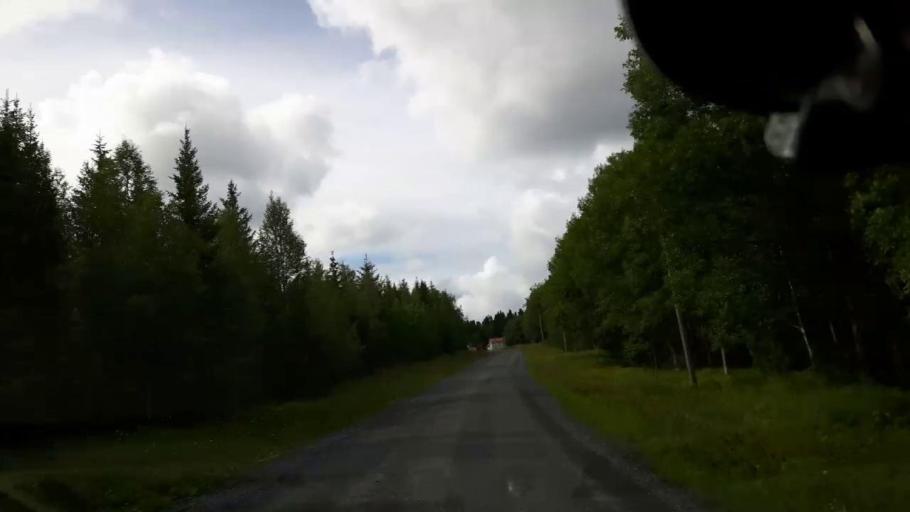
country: SE
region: Jaemtland
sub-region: Krokoms Kommun
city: Valla
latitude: 63.3566
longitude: 13.8478
